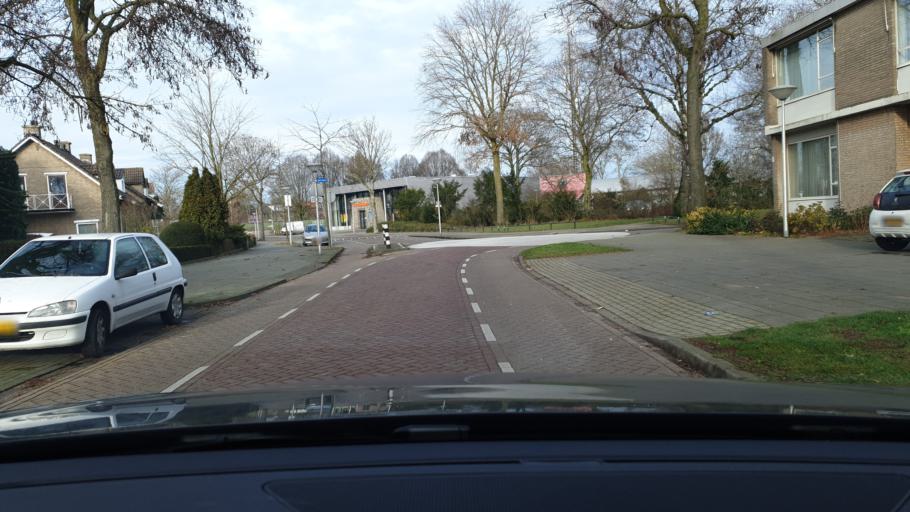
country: NL
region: North Brabant
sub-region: Gemeente Eindhoven
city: De Doornakkers
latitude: 51.4420
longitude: 5.5146
